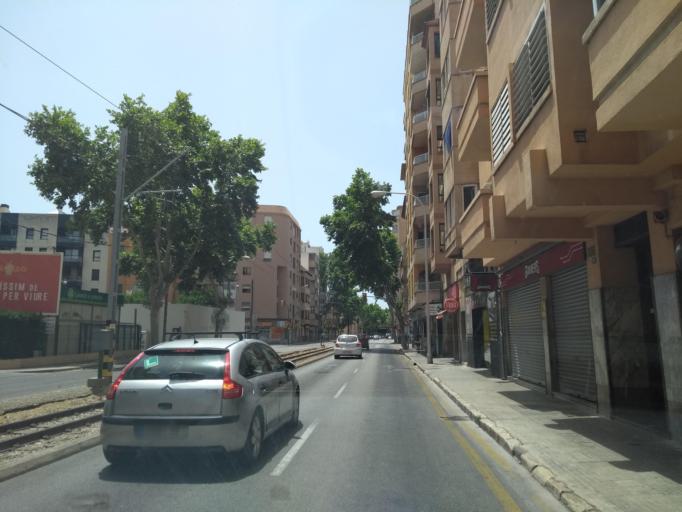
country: ES
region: Balearic Islands
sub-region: Illes Balears
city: Palma
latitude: 39.5808
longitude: 2.6592
